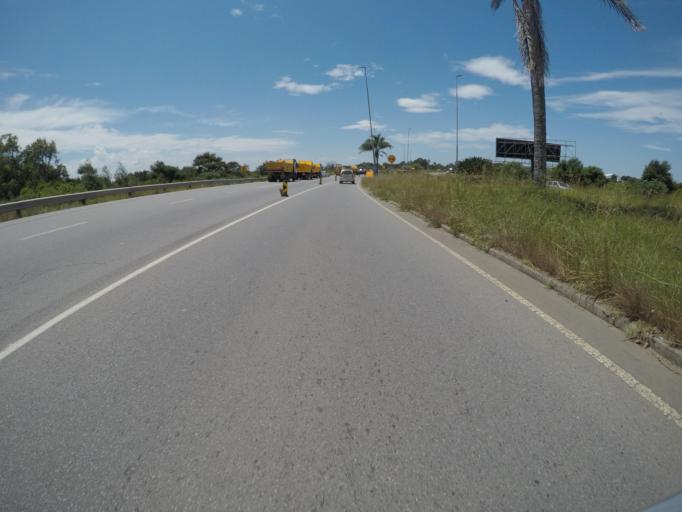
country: ZA
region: Eastern Cape
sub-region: Buffalo City Metropolitan Municipality
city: East London
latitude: -33.0372
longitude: 27.8336
